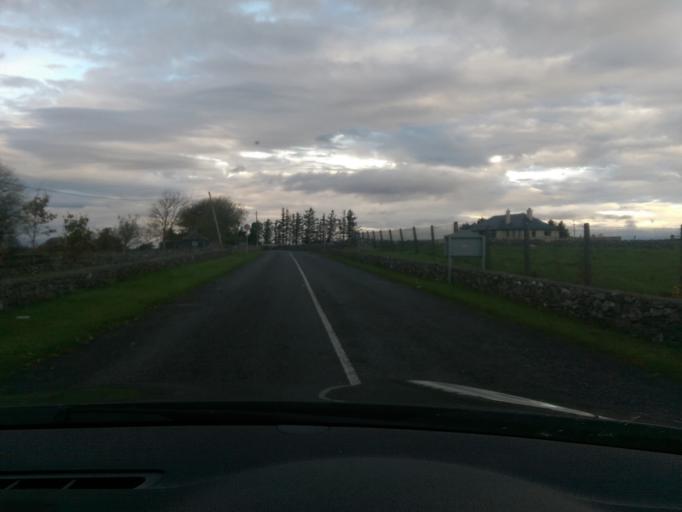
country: IE
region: Connaught
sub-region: County Galway
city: Athenry
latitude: 53.4226
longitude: -8.5723
